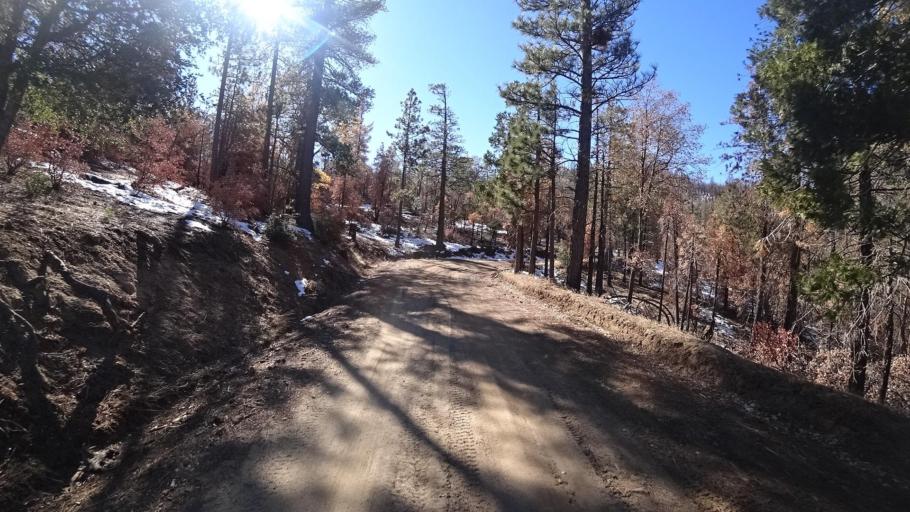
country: US
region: California
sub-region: Kern County
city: Alta Sierra
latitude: 35.7164
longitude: -118.5334
